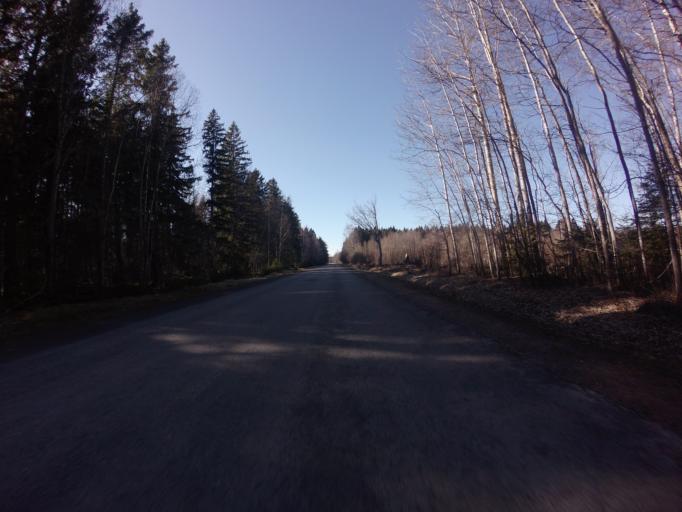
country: EE
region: Saare
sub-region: Kuressaare linn
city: Kuressaare
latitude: 58.5735
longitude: 22.6629
